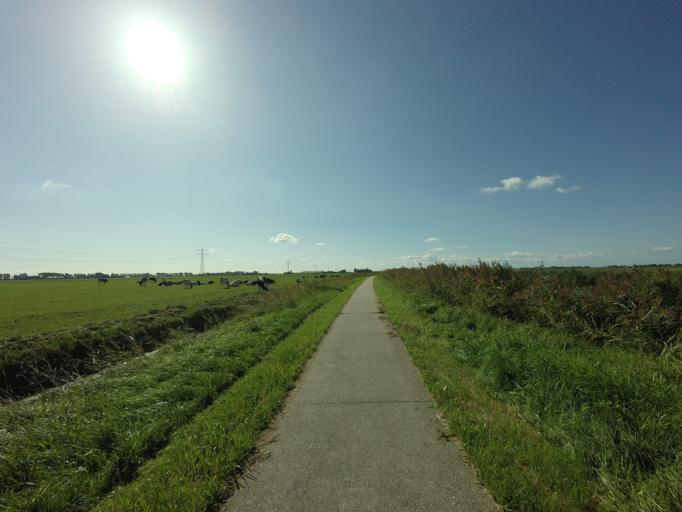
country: NL
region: Friesland
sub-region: Gemeente Boarnsterhim
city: Reduzum
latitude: 53.1441
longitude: 5.7644
